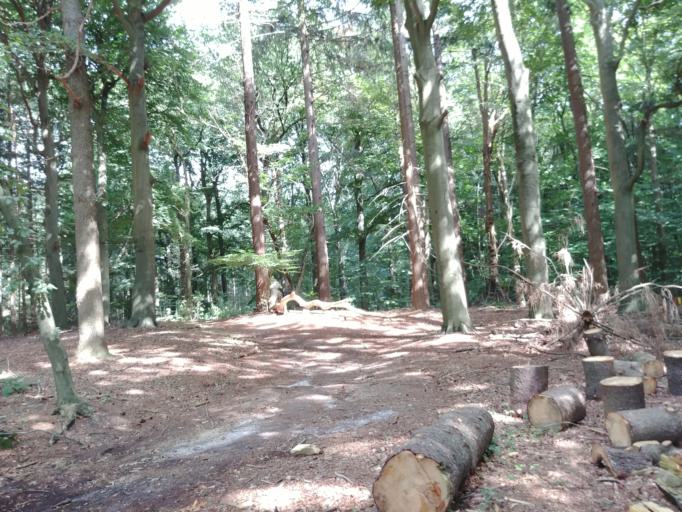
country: NL
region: Utrecht
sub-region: Gemeente Utrechtse Heuvelrug
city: Doorn
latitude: 52.0515
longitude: 5.3528
